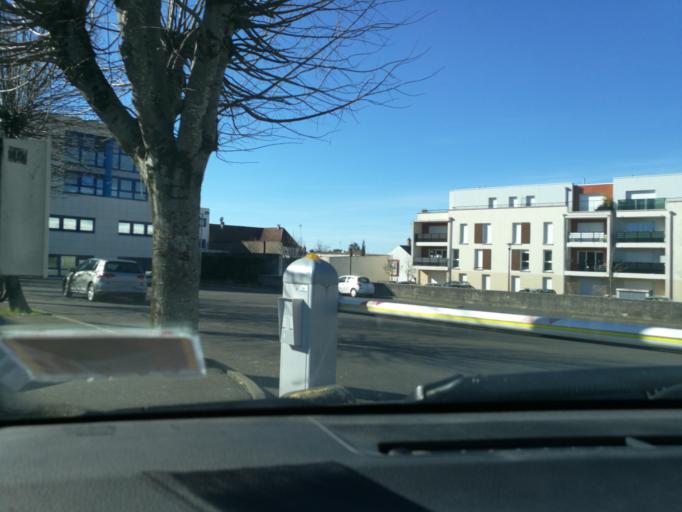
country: FR
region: Centre
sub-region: Departement du Loiret
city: Saint-Jean-de-la-Ruelle
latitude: 47.9099
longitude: 1.8839
